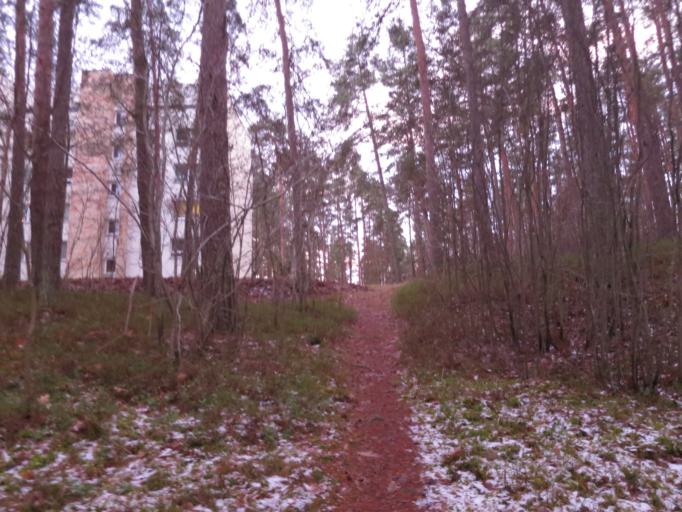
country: LV
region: Riga
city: Bergi
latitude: 56.9761
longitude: 24.3098
